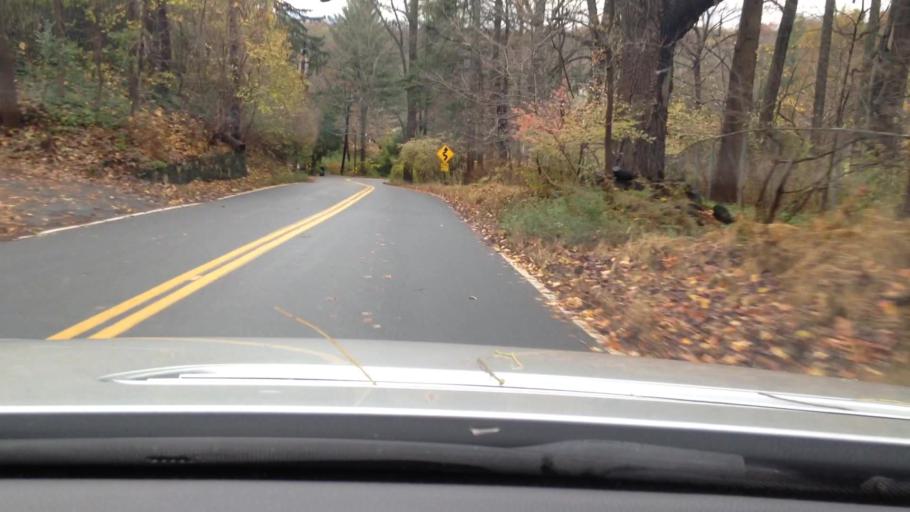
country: US
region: New York
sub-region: Westchester County
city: Croton-on-Hudson
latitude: 41.2311
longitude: -73.8862
